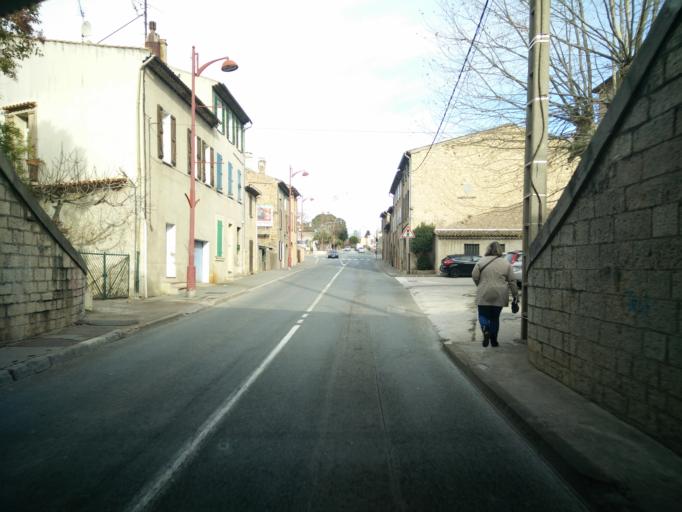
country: FR
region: Provence-Alpes-Cote d'Azur
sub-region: Departement du Var
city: Vidauban
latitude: 43.4297
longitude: 6.4344
